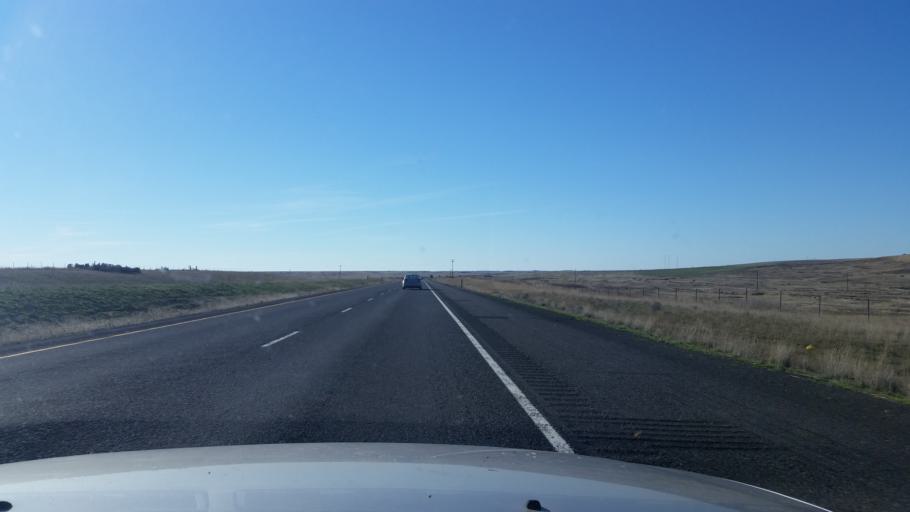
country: US
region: Washington
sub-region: Spokane County
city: Medical Lake
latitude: 47.3469
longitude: -117.9024
